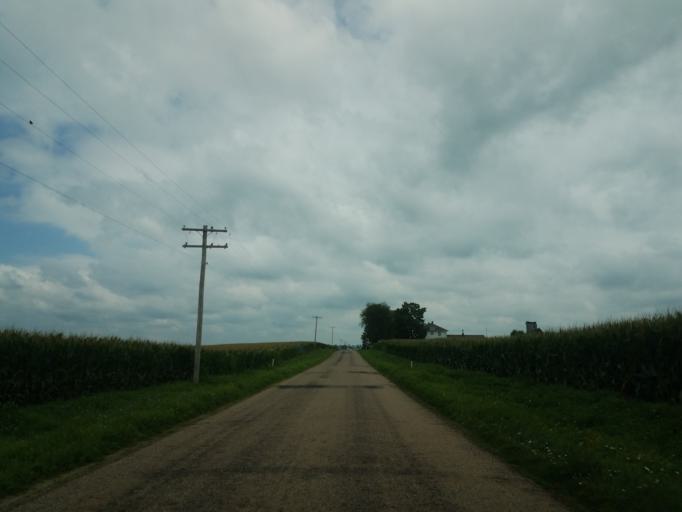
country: US
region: Illinois
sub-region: McLean County
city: Twin Grove
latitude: 40.4235
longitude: -89.0621
